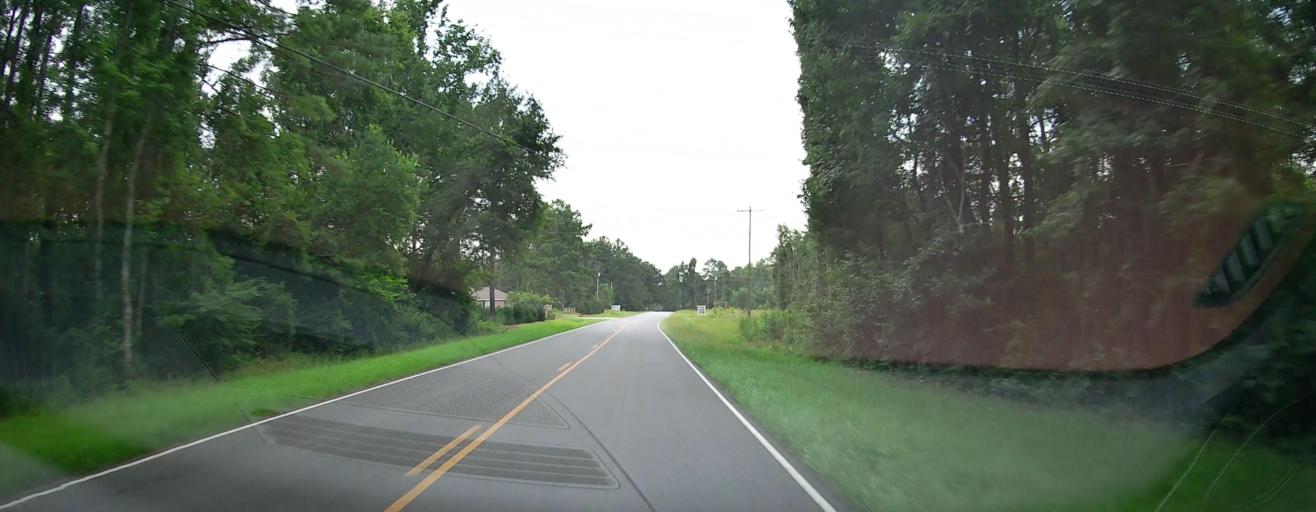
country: US
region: Georgia
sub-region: Laurens County
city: Dublin
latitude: 32.5855
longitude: -82.9019
